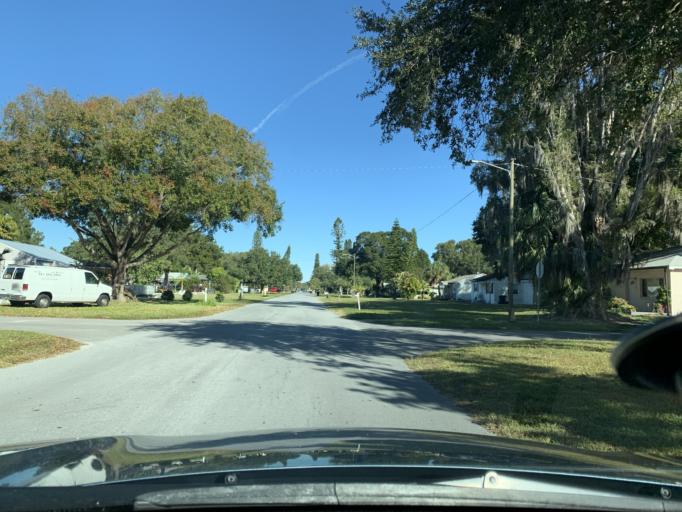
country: US
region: Florida
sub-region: Pinellas County
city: Gulfport
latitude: 27.7561
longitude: -82.7079
